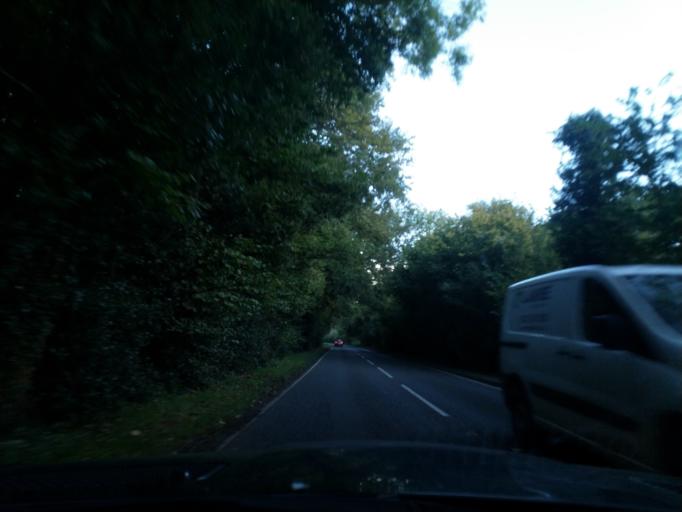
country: GB
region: England
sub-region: Solihull
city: Cheswick Green
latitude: 52.3499
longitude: -1.7753
